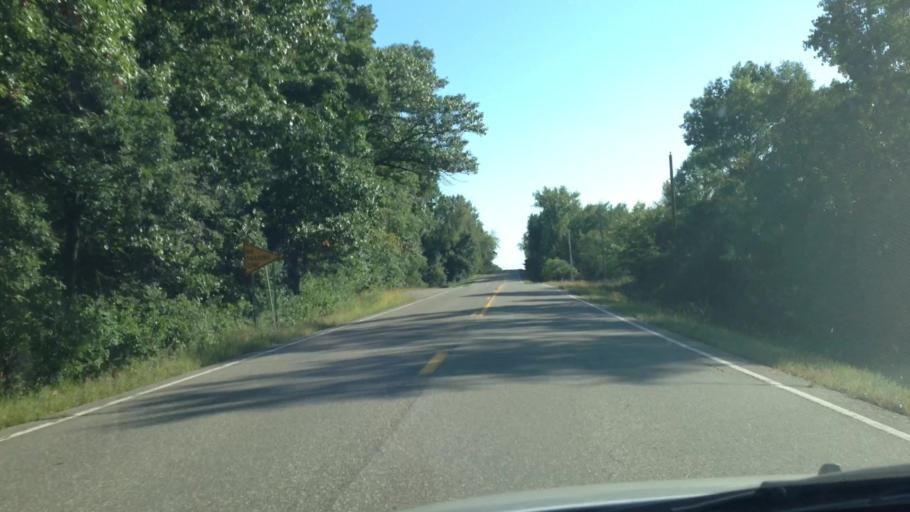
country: US
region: Minnesota
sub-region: Washington County
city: Stillwater
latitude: 45.1145
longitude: -92.8128
